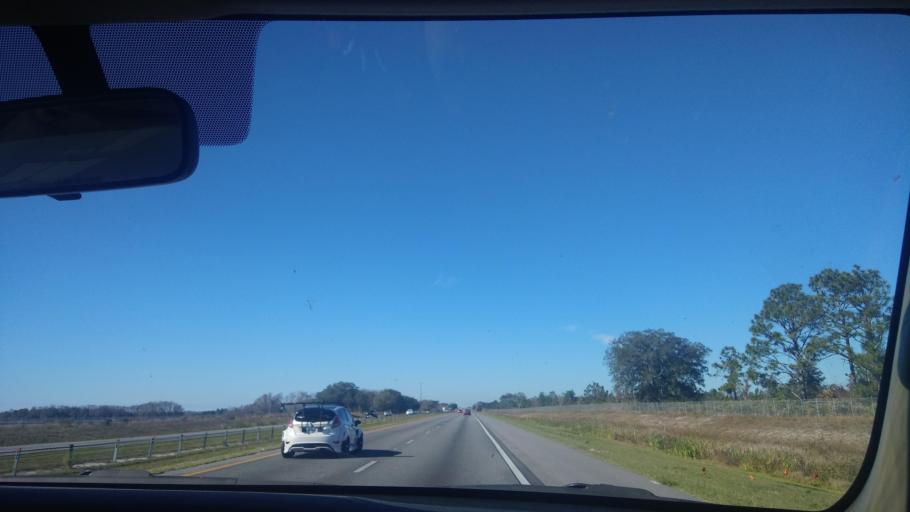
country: US
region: Florida
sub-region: Orange County
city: Wedgefield
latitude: 28.4517
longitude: -81.1262
